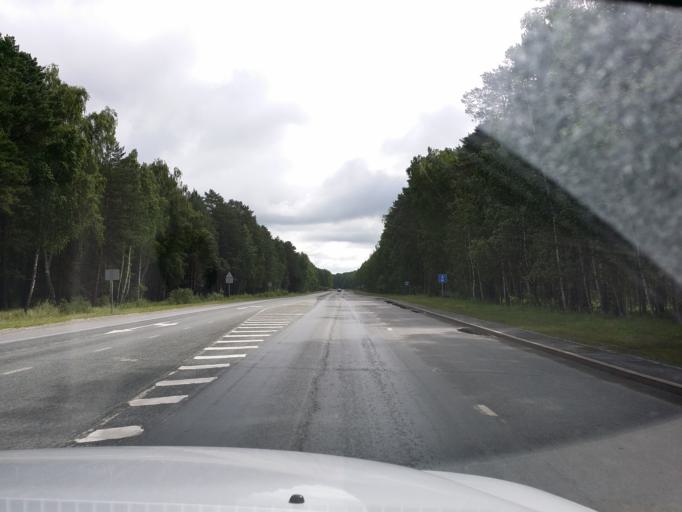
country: RU
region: Tjumen
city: Yalutorovsk
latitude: 57.1571
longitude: 66.5054
